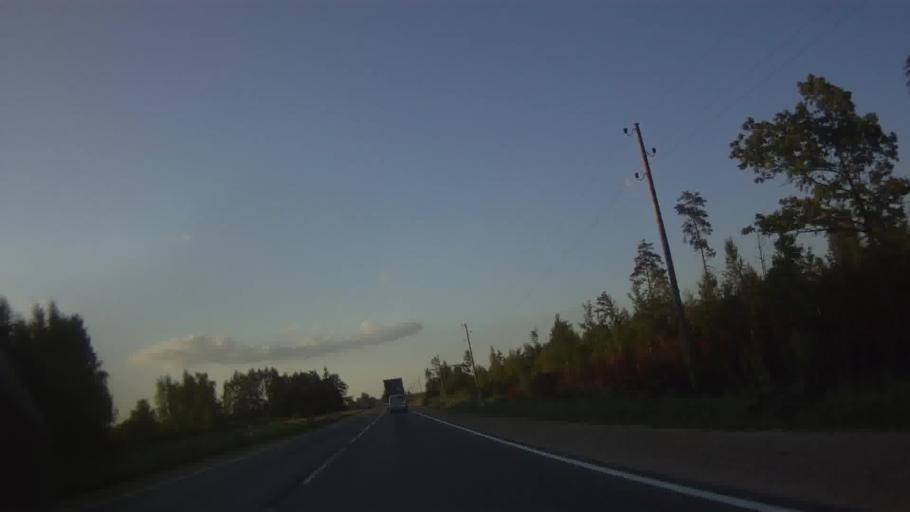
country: LV
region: Salas
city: Sala
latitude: 56.5673
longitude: 25.7751
